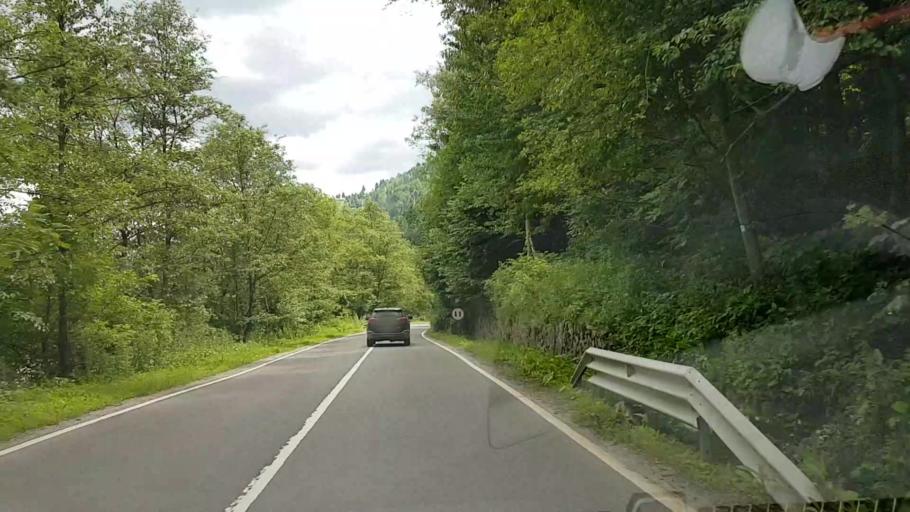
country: RO
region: Neamt
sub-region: Comuna Farcasa
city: Farcasa
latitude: 47.1380
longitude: 25.8619
